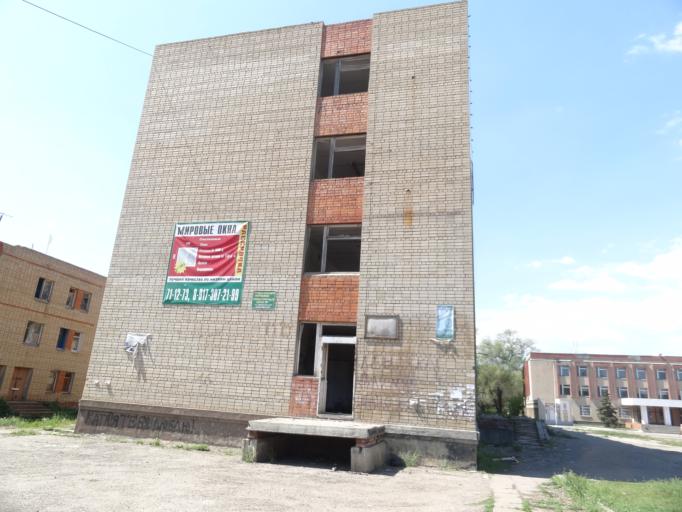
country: RU
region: Saratov
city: Privolzhskiy
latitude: 51.3897
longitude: 46.1272
